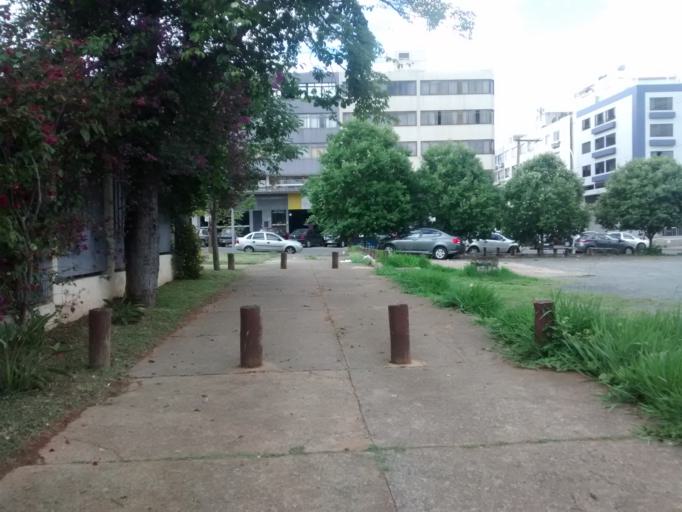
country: BR
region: Federal District
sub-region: Brasilia
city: Brasilia
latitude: -15.7519
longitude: -47.8957
